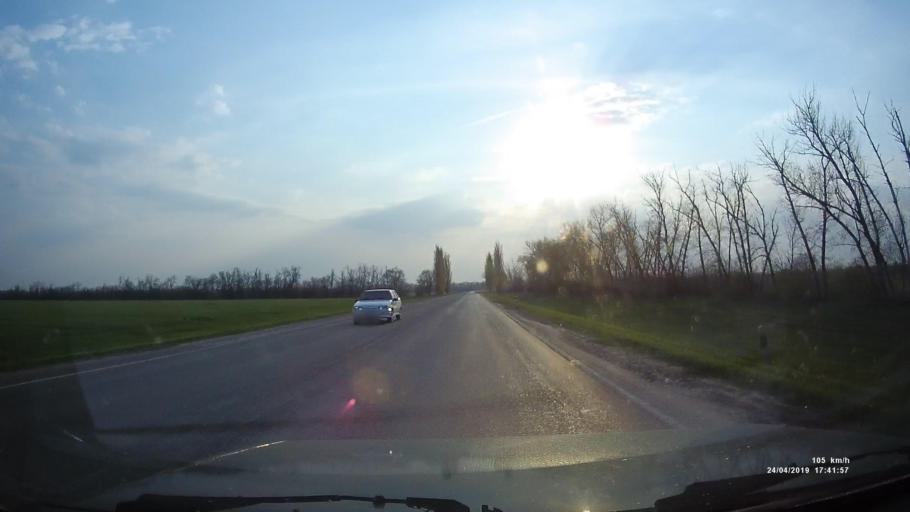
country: RU
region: Rostov
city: Tselina
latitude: 46.5312
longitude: 40.9588
